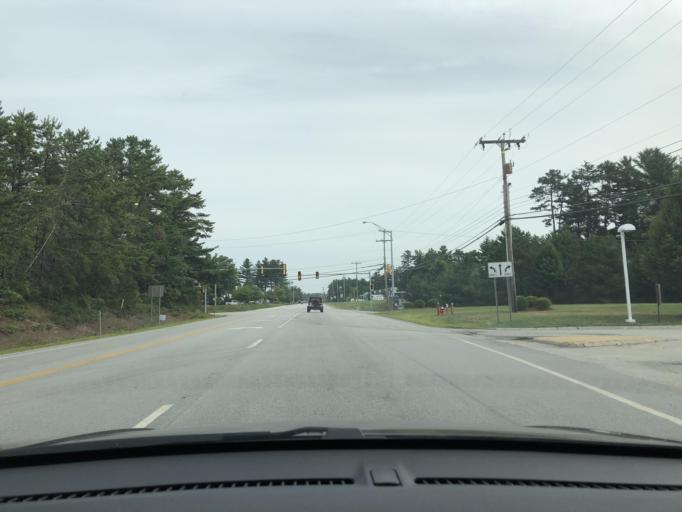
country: US
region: New Hampshire
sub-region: Merrimack County
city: Concord
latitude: 43.2123
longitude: -71.4833
